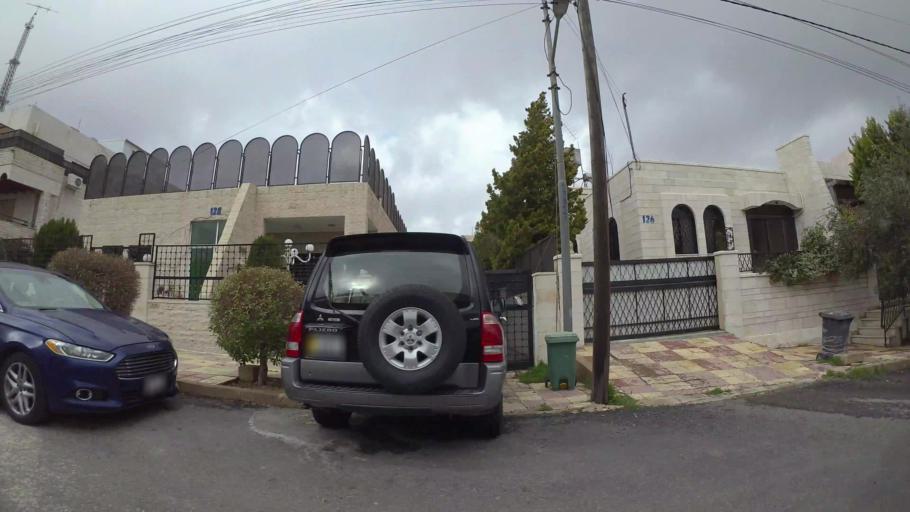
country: JO
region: Amman
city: Amman
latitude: 31.9416
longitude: 35.9020
